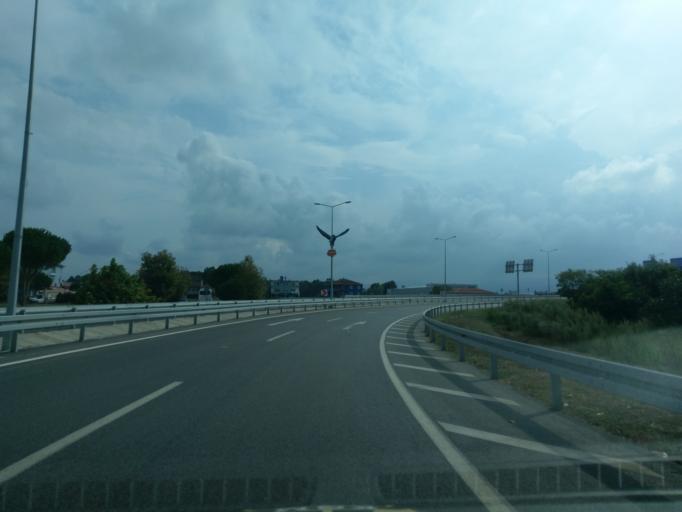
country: TR
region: Samsun
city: Dikbiyik
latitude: 41.2391
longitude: 36.5396
